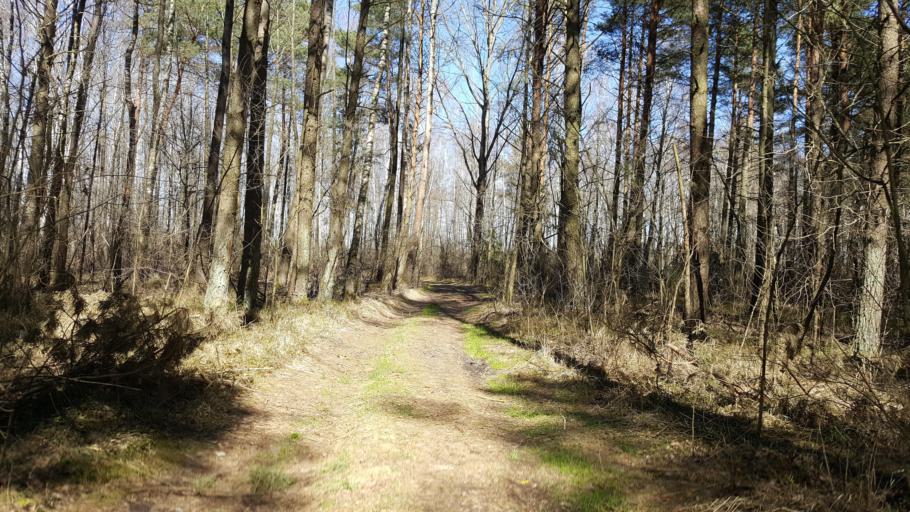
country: BY
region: Brest
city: Zhabinka
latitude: 52.2425
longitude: 23.9532
